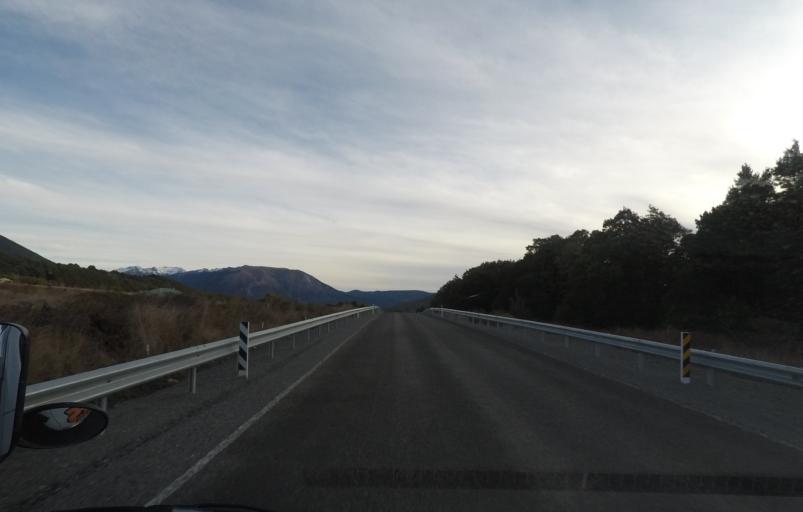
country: NZ
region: Tasman
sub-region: Tasman District
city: Wakefield
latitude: -41.7860
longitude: 172.8916
